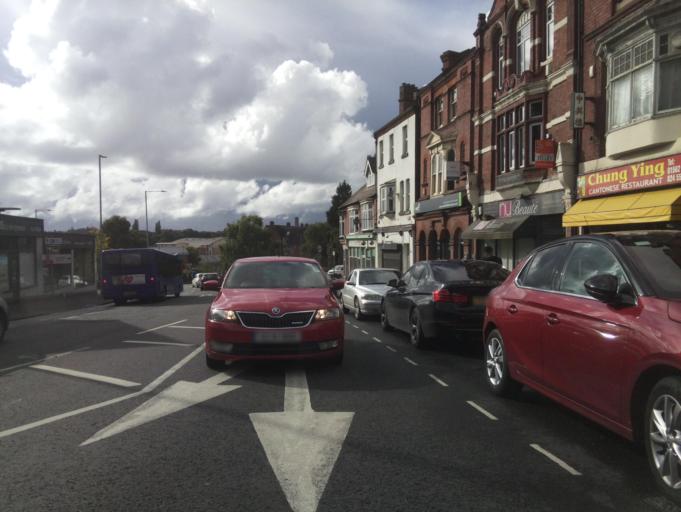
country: GB
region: England
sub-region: Worcestershire
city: Kidderminster
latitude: 52.3855
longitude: -2.2423
